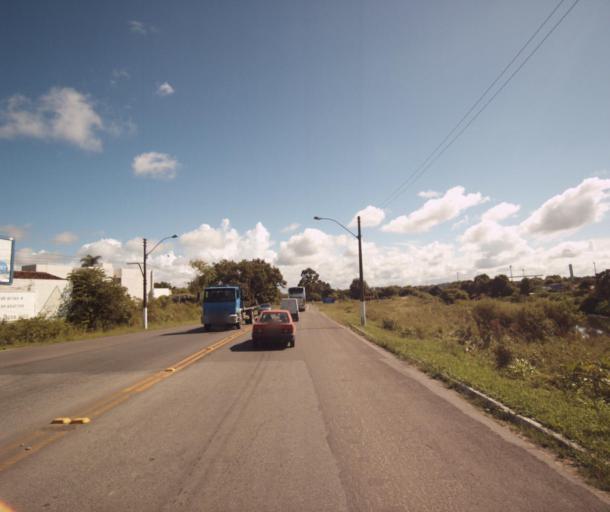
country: BR
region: Rio Grande do Sul
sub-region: Pelotas
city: Pelotas
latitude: -31.7631
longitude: -52.3563
